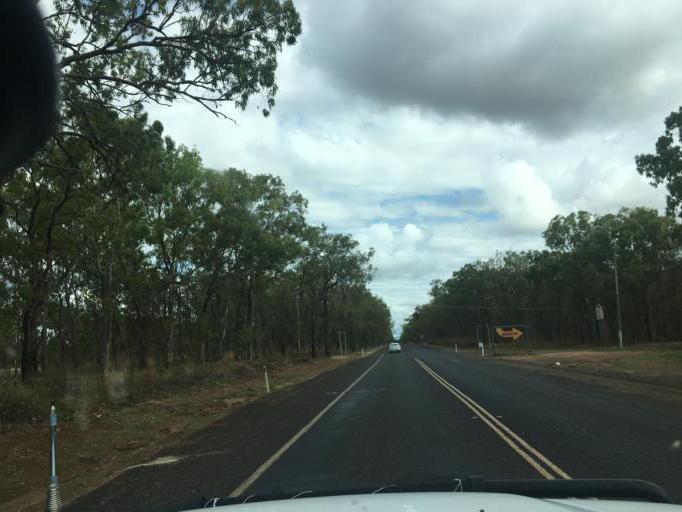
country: AU
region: Queensland
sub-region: Tablelands
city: Mareeba
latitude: -17.0487
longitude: 145.4309
